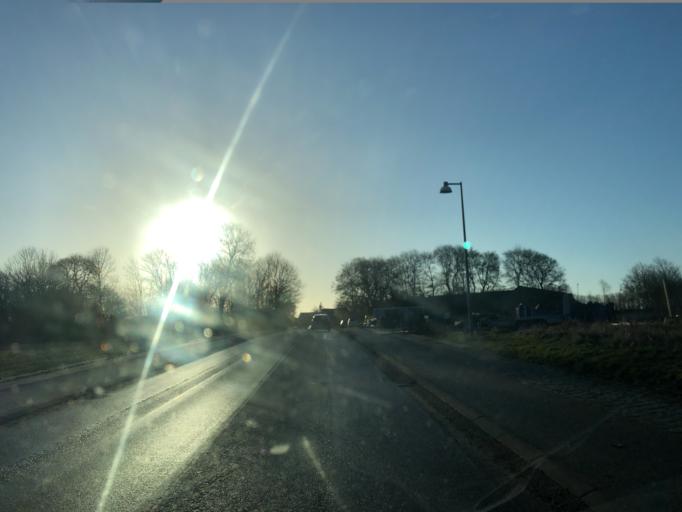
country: DK
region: Central Jutland
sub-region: Favrskov Kommune
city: Hinnerup
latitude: 56.2481
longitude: 10.0372
